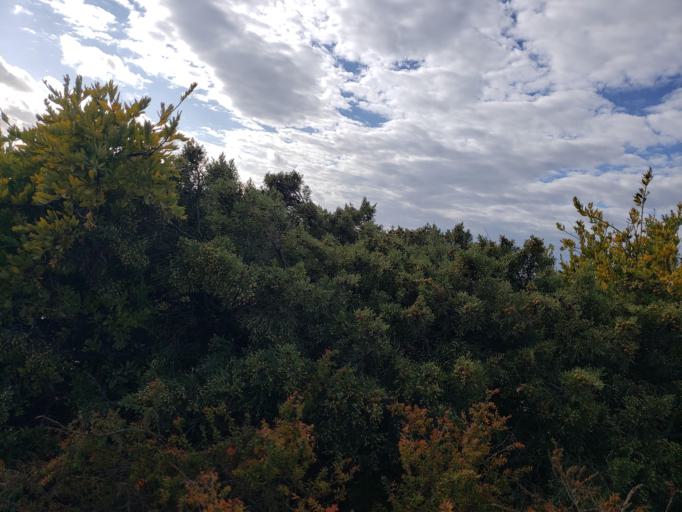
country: PT
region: Faro
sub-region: Lagos
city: Lagos
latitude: 37.0796
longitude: -8.6686
